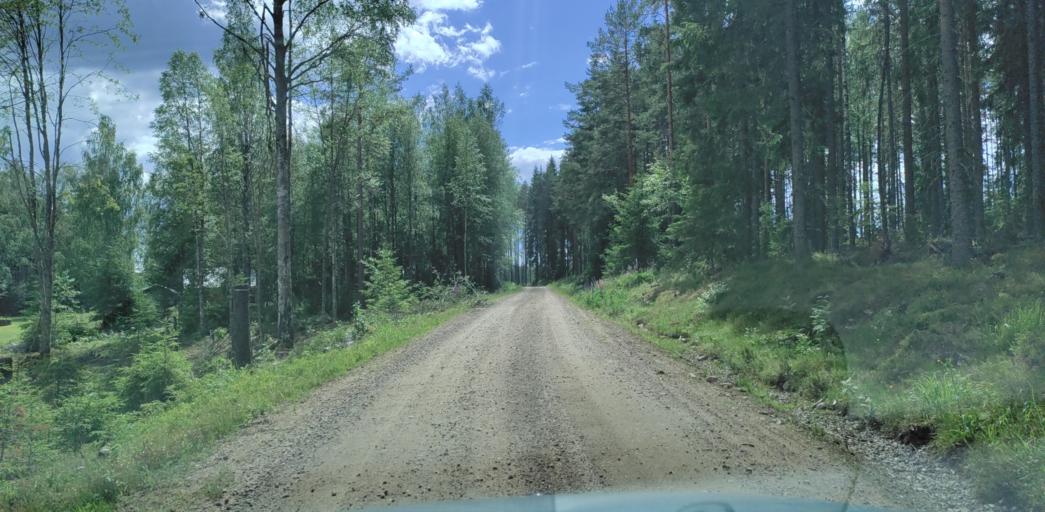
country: SE
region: Vaermland
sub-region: Hagfors Kommun
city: Ekshaerad
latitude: 60.0514
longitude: 13.3104
